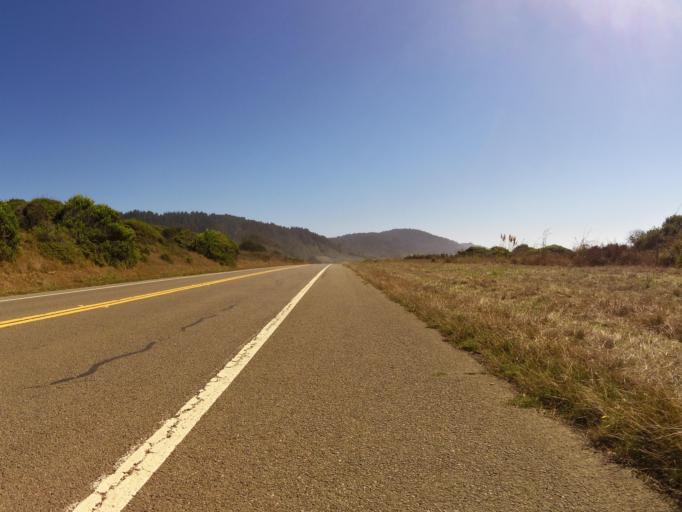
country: US
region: California
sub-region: Mendocino County
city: Fort Bragg
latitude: 39.6676
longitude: -123.7896
